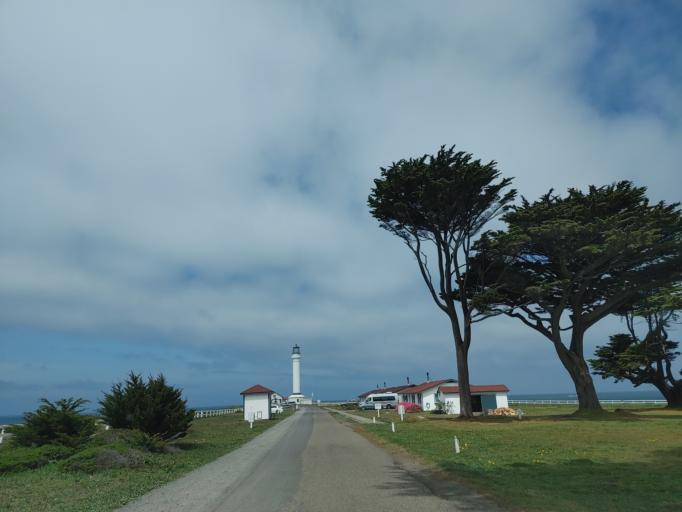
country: US
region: California
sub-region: Sonoma County
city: Sea Ranch
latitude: 38.9529
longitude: -123.7380
